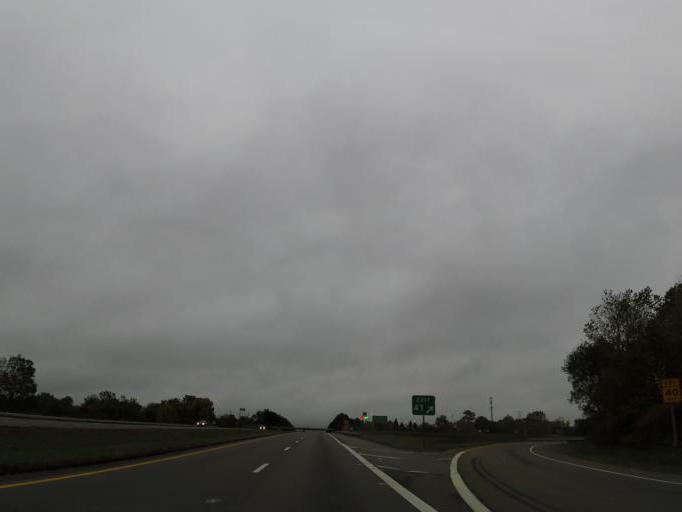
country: US
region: Virginia
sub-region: Wythe County
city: Wytheville
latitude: 36.9717
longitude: -81.0675
